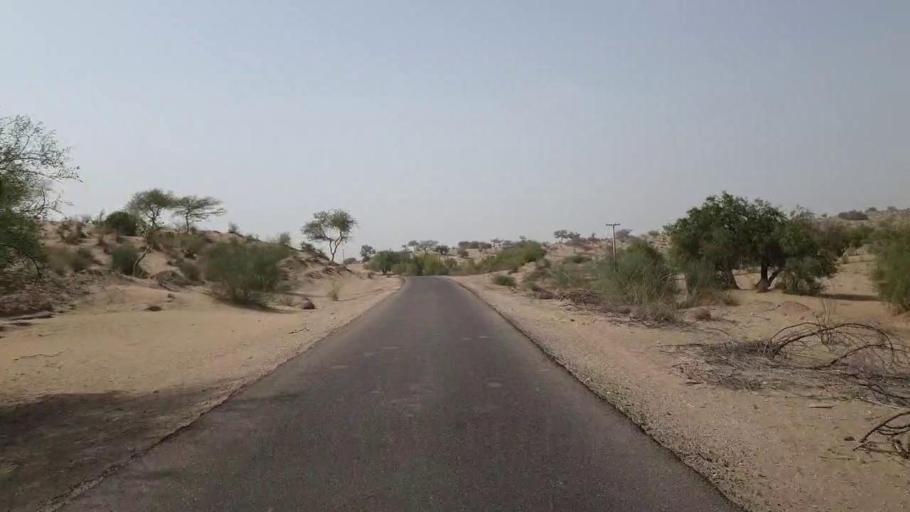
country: PK
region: Sindh
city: Mithi
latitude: 24.5959
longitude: 69.9249
